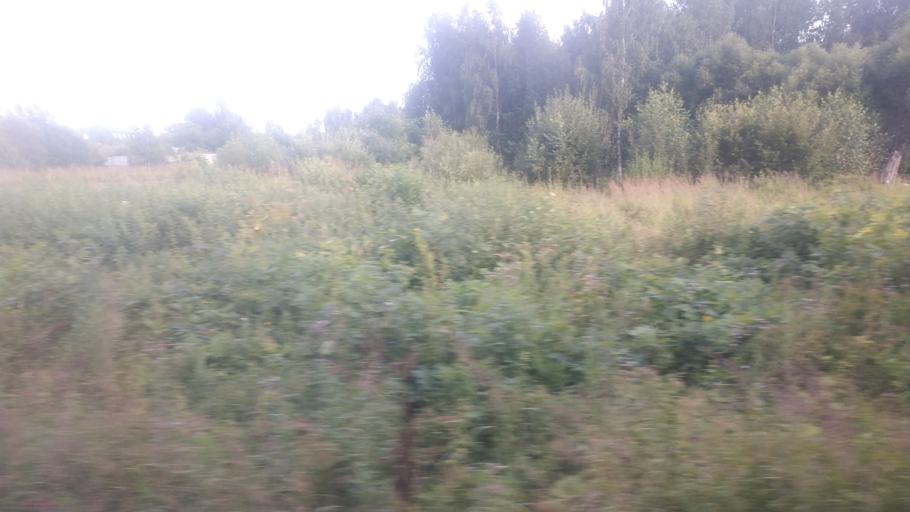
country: RU
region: Moskovskaya
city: Tugolesskiy Bor
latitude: 55.5527
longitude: 39.6956
